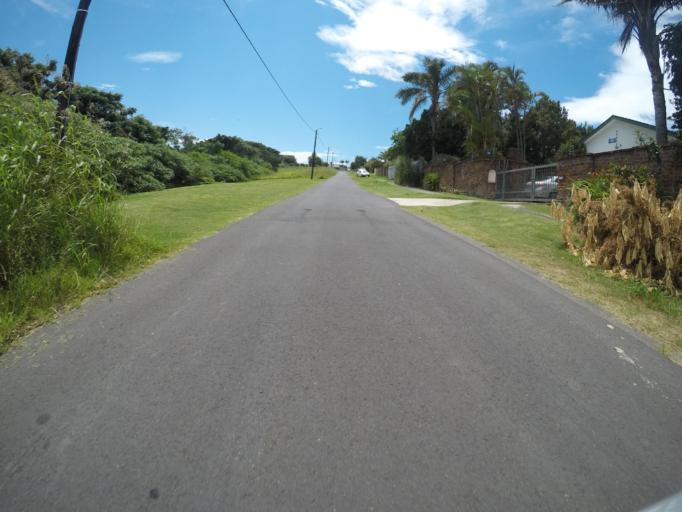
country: ZA
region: Eastern Cape
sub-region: Buffalo City Metropolitan Municipality
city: East London
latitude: -33.0396
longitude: 27.8483
